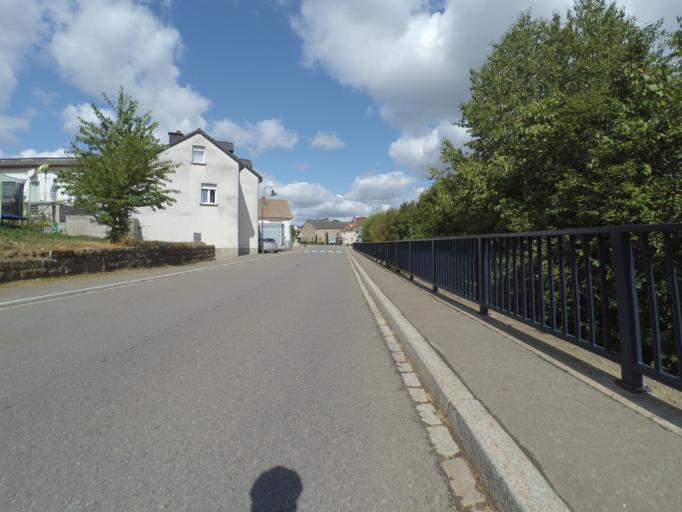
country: LU
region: Grevenmacher
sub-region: Canton de Grevenmacher
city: Flaxweiler
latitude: 49.6290
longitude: 6.3365
